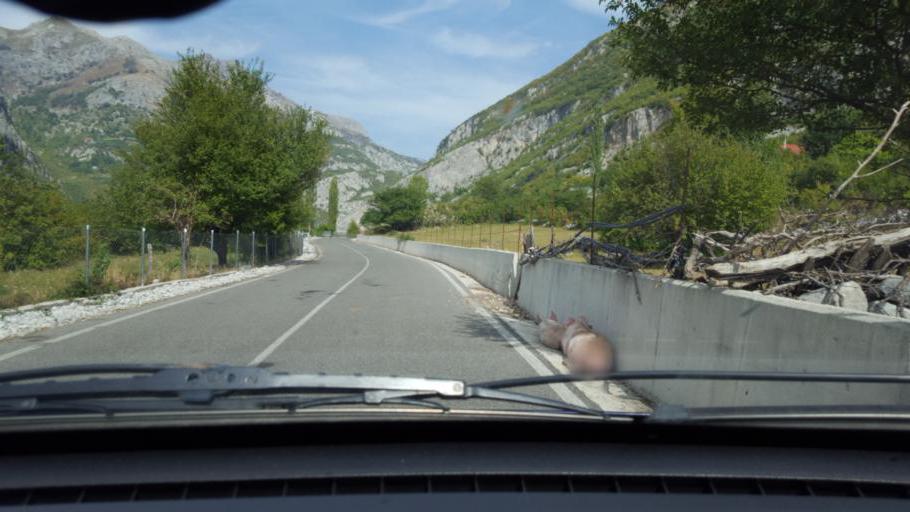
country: AL
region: Shkoder
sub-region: Rrethi i Malesia e Madhe
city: Kastrat
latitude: 42.5128
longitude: 19.6193
